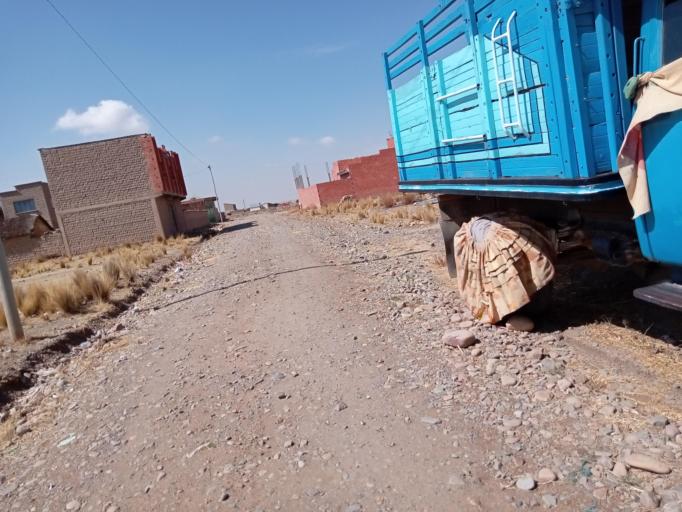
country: BO
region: La Paz
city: Batallas
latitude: -16.4386
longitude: -68.3739
